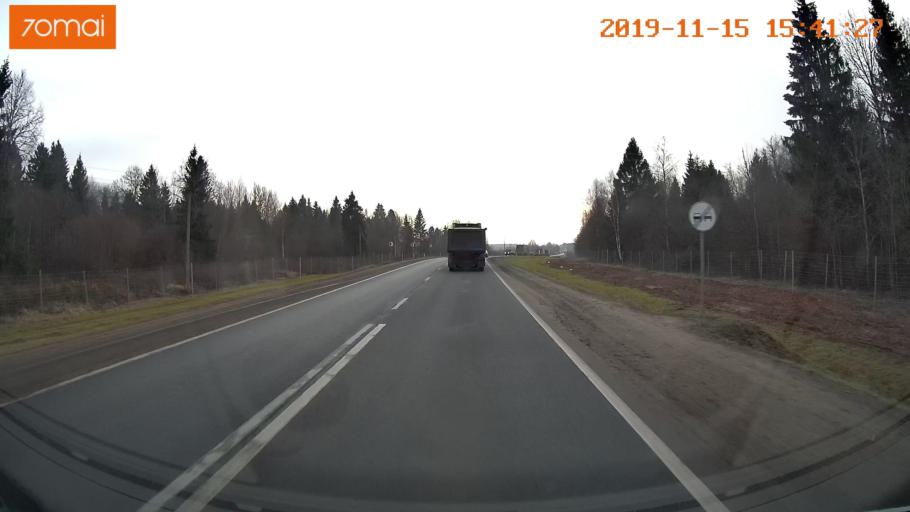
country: RU
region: Jaroslavl
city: Danilov
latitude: 58.0005
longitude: 40.0480
